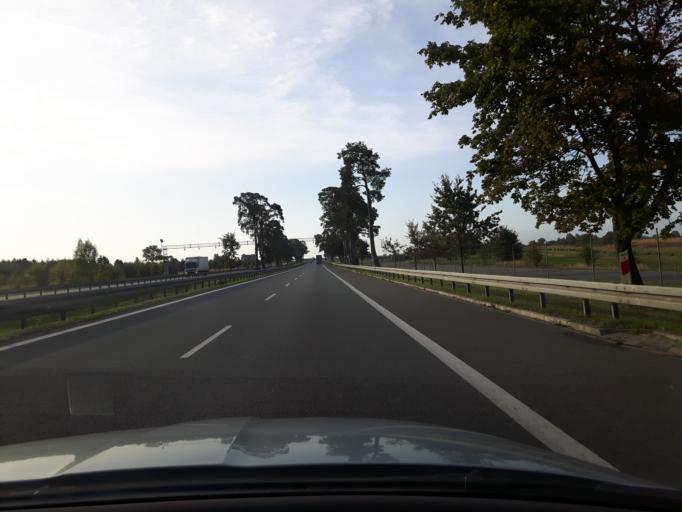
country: PL
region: Masovian Voivodeship
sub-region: Powiat bialobrzeski
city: Stara Blotnica
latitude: 51.5914
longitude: 20.9947
